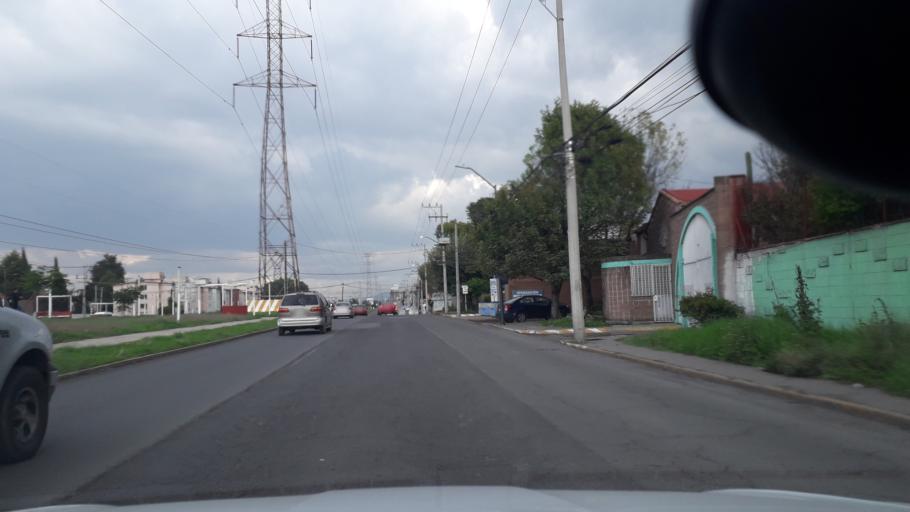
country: MX
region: Mexico
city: Santiago Teyahualco
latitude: 19.6412
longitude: -99.1223
